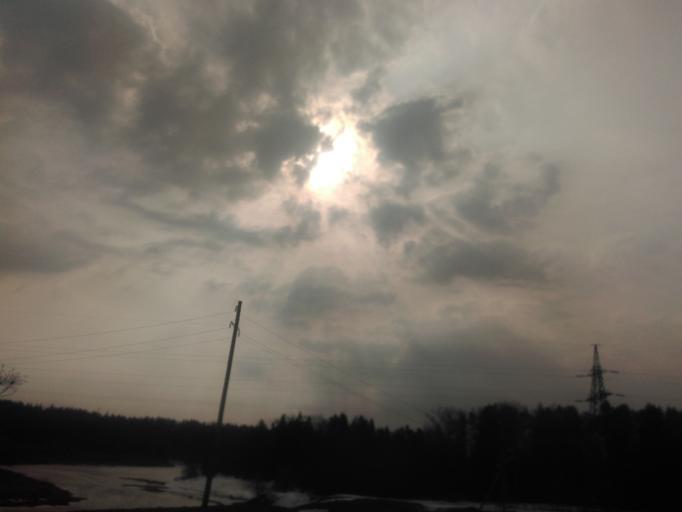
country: RU
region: Moskovskaya
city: Tuchkovo
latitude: 55.6108
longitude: 36.4209
